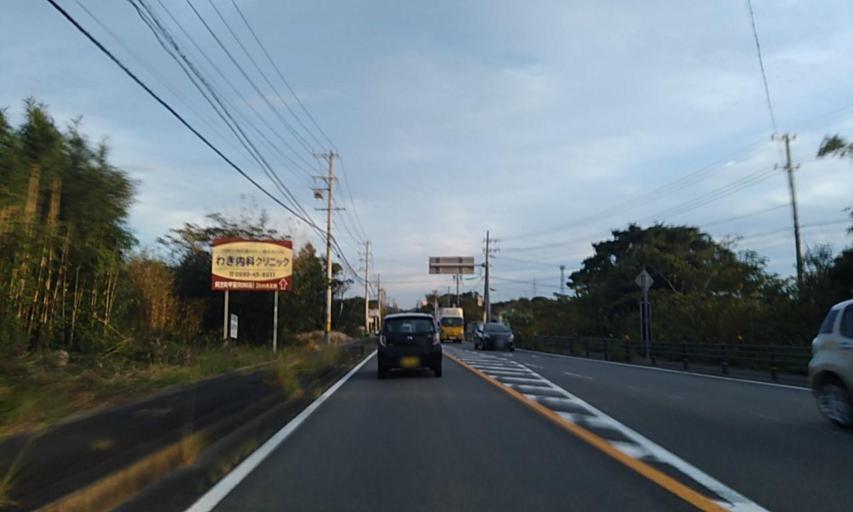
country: JP
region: Mie
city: Toba
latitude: 34.3192
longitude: 136.8539
